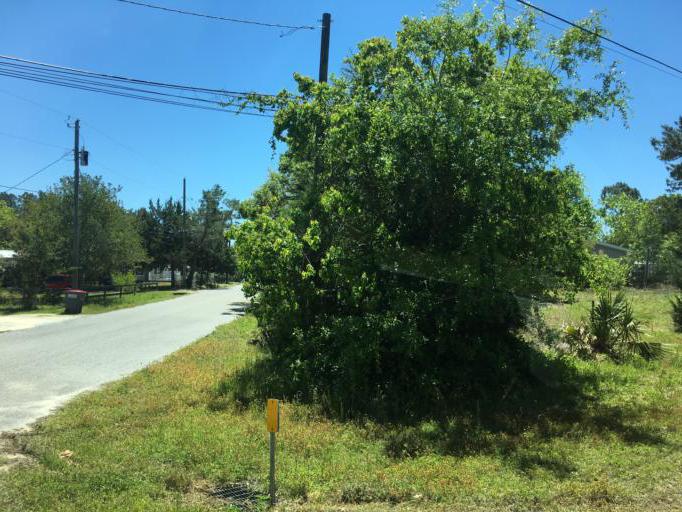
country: US
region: Florida
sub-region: Bay County
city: Laguna Beach
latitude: 30.2564
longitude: -85.9392
